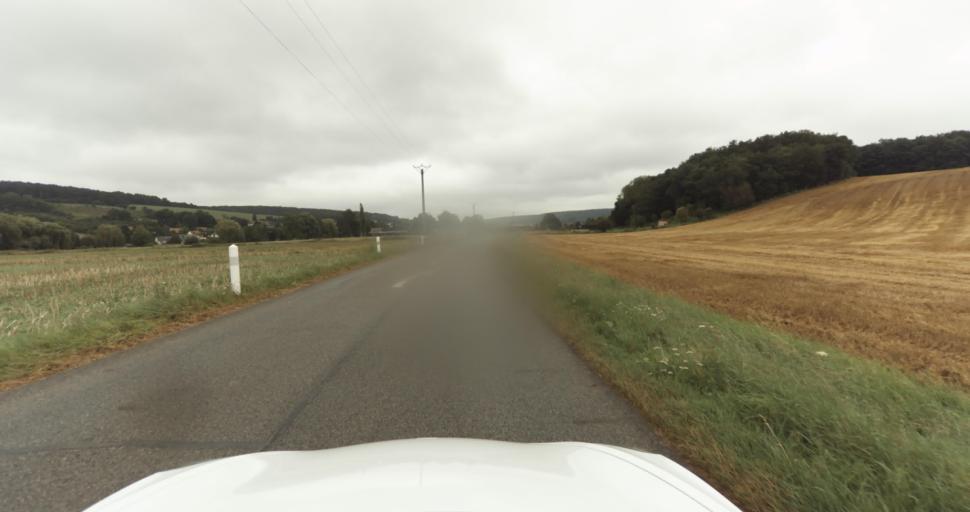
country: FR
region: Haute-Normandie
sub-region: Departement de l'Eure
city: Normanville
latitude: 49.0954
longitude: 1.1361
